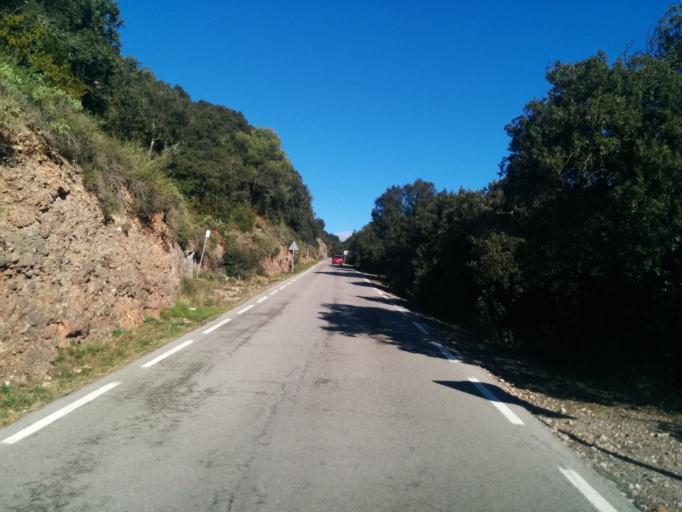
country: ES
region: Catalonia
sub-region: Provincia de Barcelona
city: Mura
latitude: 41.6636
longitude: 1.9931
